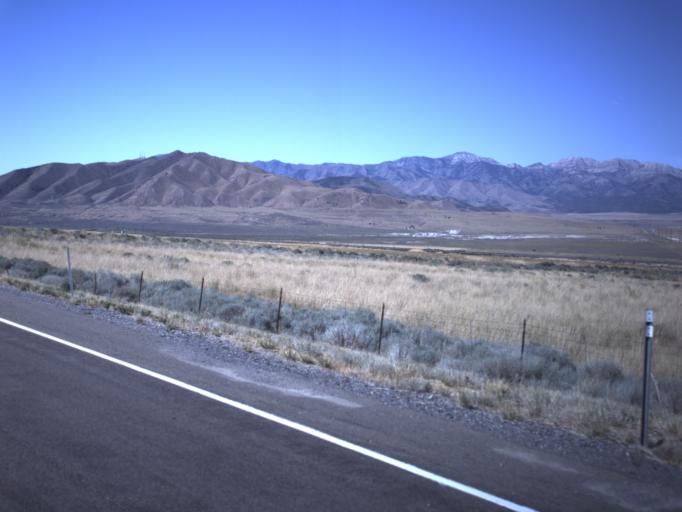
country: US
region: Utah
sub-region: Tooele County
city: Tooele
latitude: 40.4905
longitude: -112.3343
